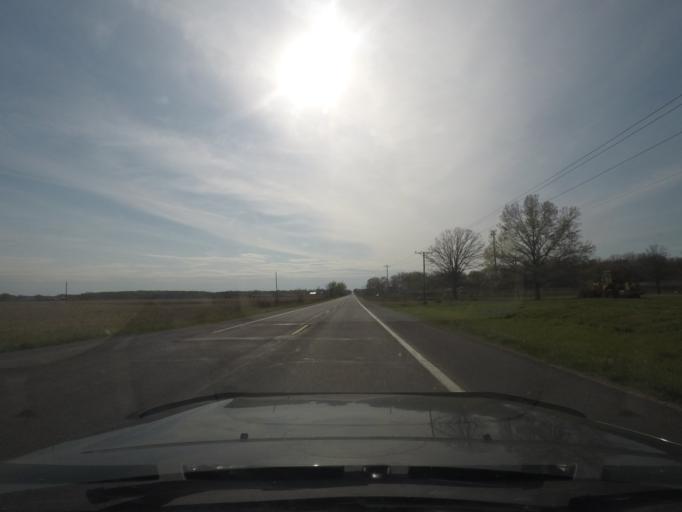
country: US
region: Michigan
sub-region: Berrien County
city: Three Oaks
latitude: 41.7985
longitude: -86.5813
